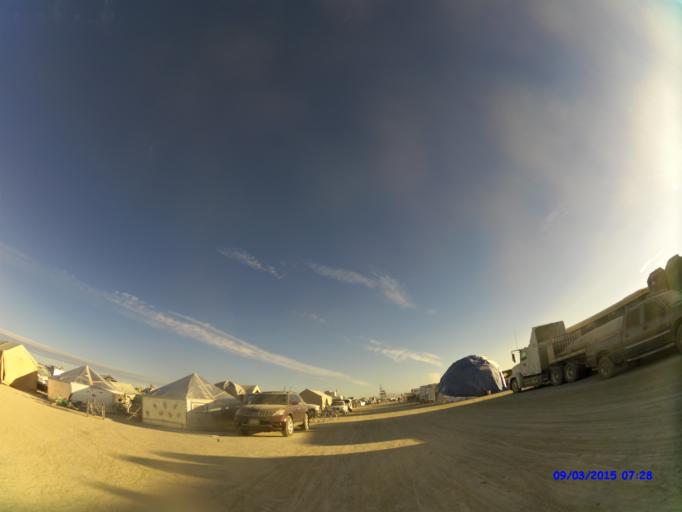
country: US
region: Nevada
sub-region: Pershing County
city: Lovelock
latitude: 40.7875
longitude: -119.2170
